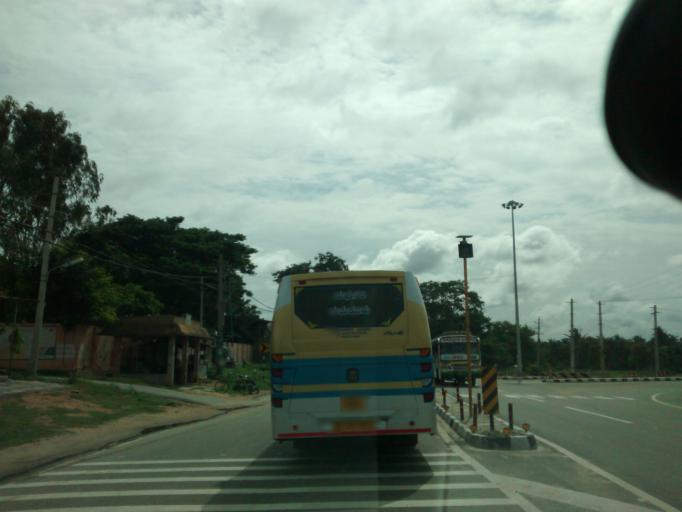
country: IN
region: Karnataka
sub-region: Tumkur
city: Koratagere
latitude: 13.5114
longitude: 77.2221
